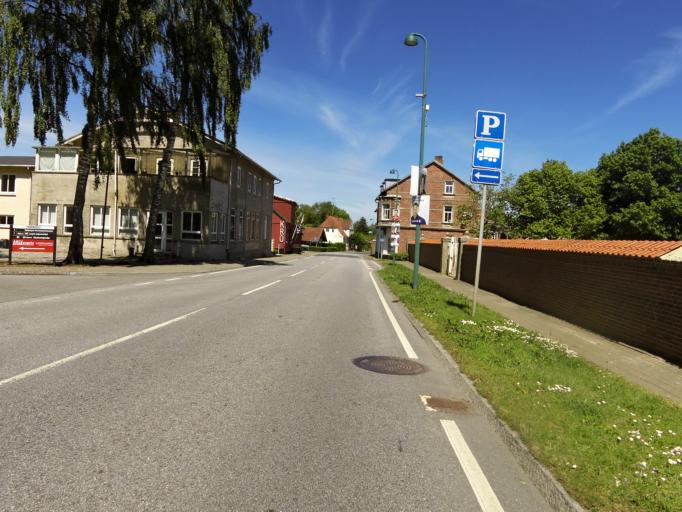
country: DK
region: South Denmark
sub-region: Haderslev Kommune
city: Gram
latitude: 55.2941
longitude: 9.0546
